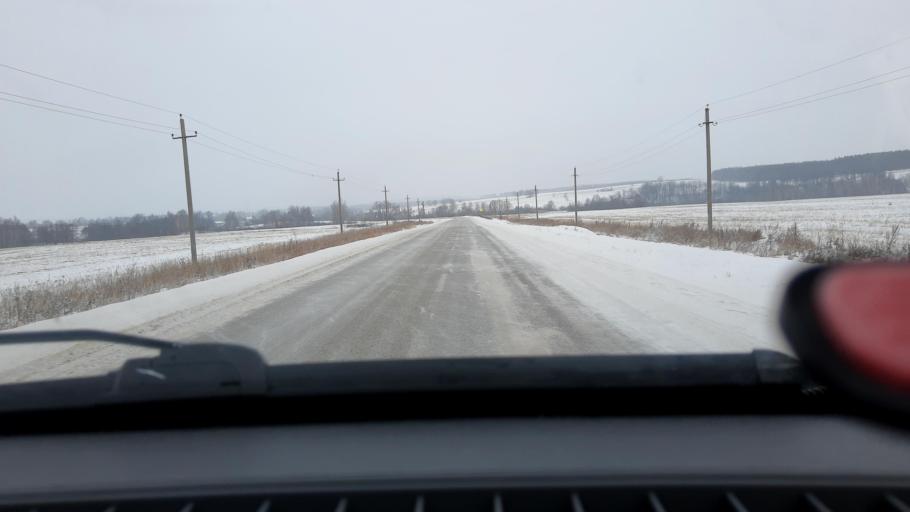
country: RU
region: Bashkortostan
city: Iglino
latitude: 54.6959
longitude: 56.4164
